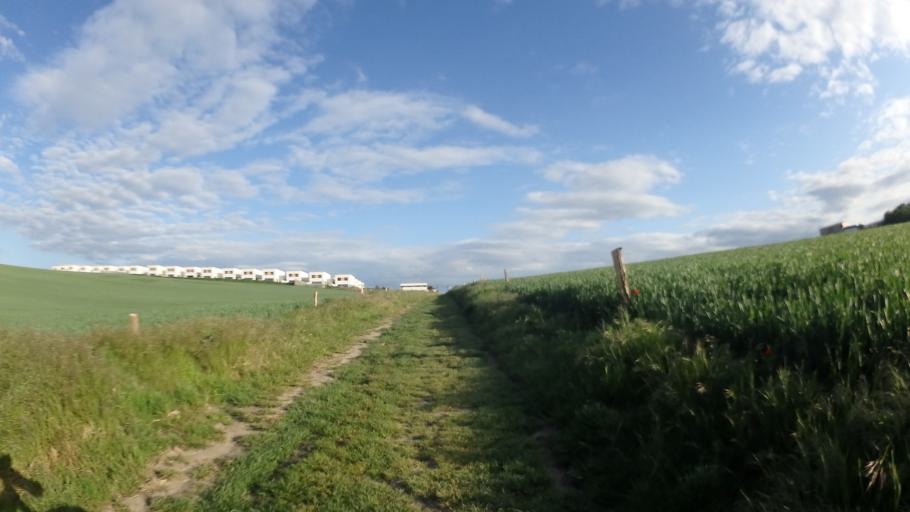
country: CZ
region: South Moravian
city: Moravany
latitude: 49.1533
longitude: 16.5783
